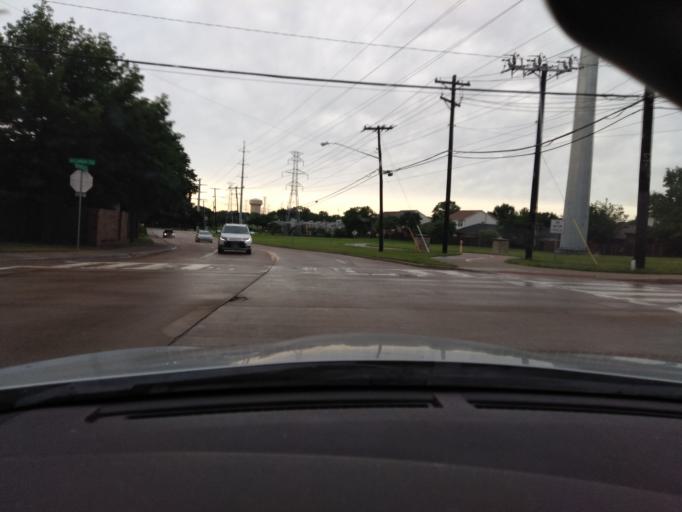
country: US
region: Texas
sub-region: Dallas County
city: Addison
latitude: 32.9879
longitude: -96.7786
